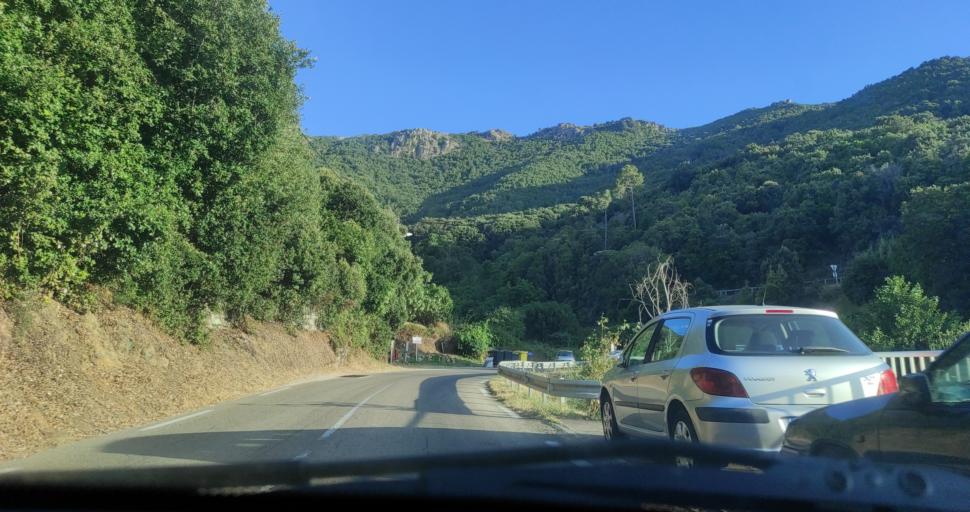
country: FR
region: Corsica
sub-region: Departement de la Corse-du-Sud
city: Appietto
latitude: 42.0301
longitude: 8.7599
